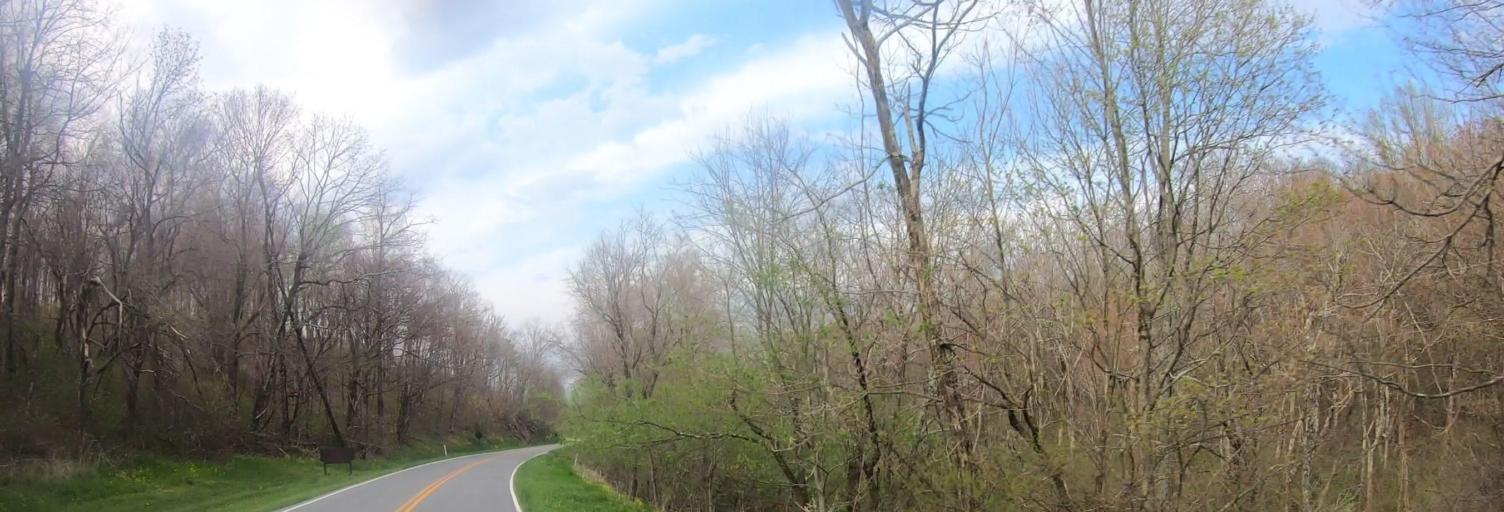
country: US
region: Virginia
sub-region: Rockingham County
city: Elkton
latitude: 38.2635
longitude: -78.6602
